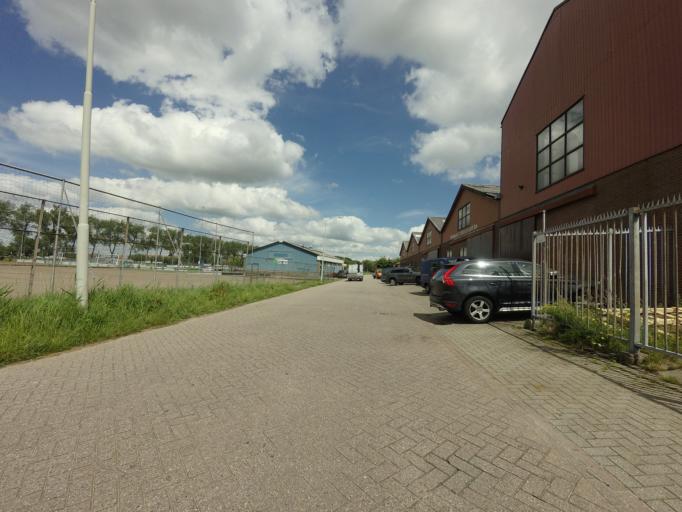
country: NL
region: North Holland
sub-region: Gemeente Zaanstad
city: Zaanstad
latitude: 52.4704
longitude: 4.8178
